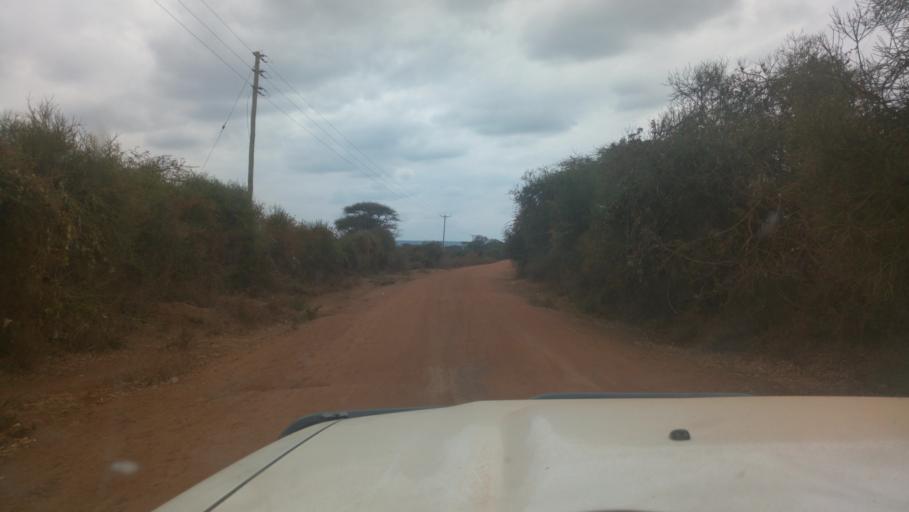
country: KE
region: Kitui
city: Kitui
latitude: -1.6086
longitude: 37.8776
